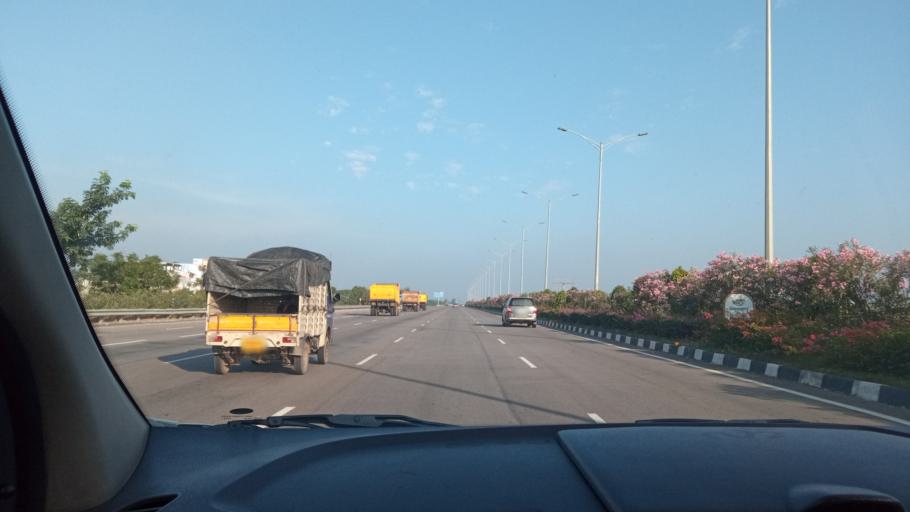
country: IN
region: Telangana
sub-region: Hyderabad
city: Hyderabad
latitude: 17.3419
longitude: 78.3644
